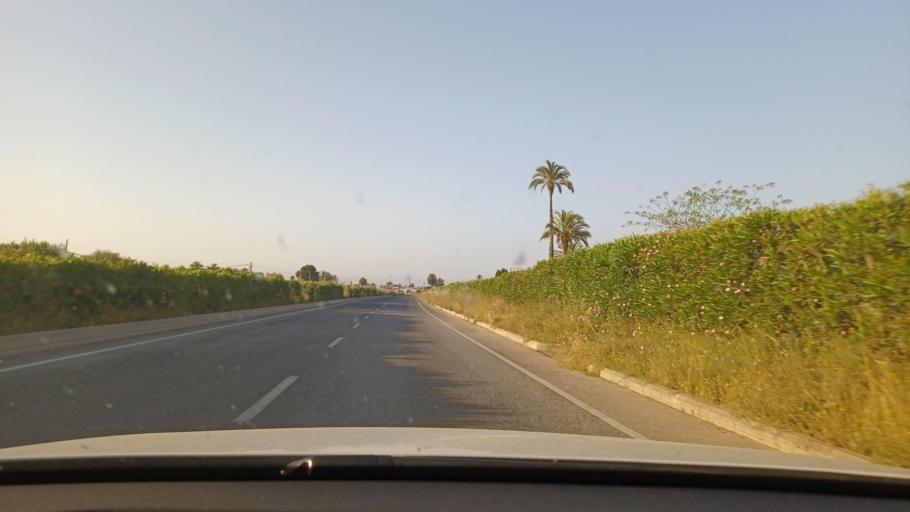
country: ES
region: Valencia
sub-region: Provincia de Alicante
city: Elche
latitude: 38.2300
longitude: -0.6997
